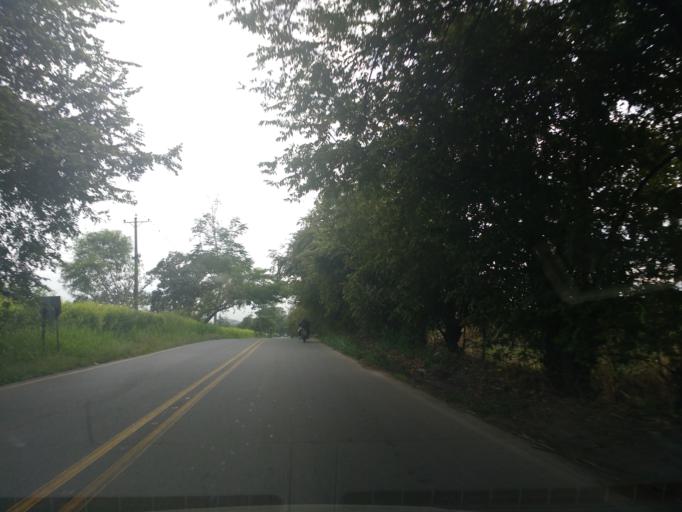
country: CO
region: Valle del Cauca
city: Florida
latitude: 3.3004
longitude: -76.2313
